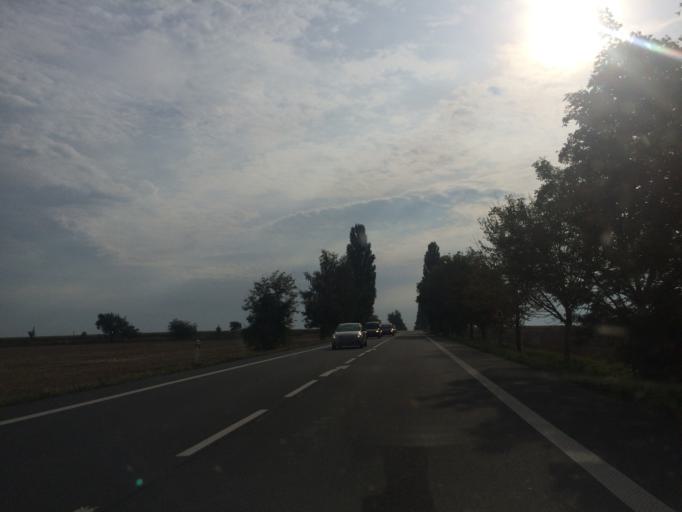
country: CZ
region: Central Bohemia
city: Poricany
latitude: 50.0513
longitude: 14.9320
